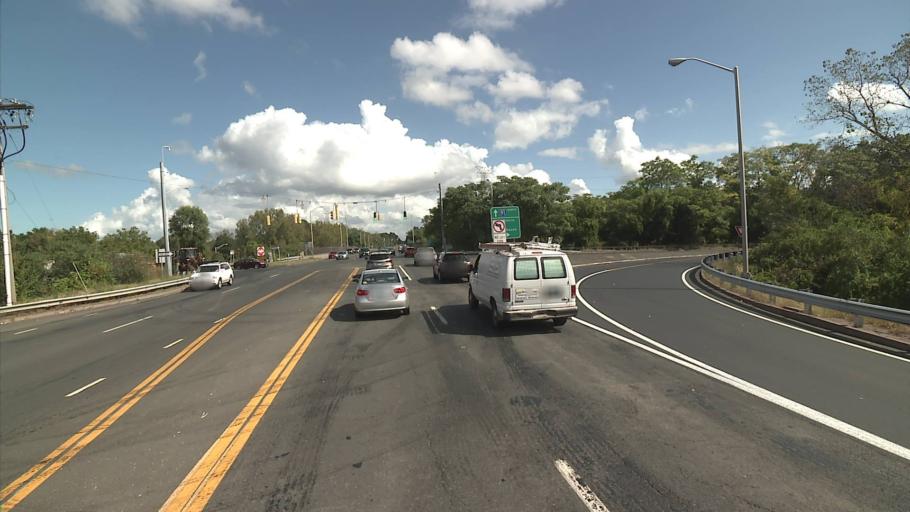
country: US
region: Connecticut
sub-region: Middlesex County
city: Cromwell
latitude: 41.6503
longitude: -72.6740
